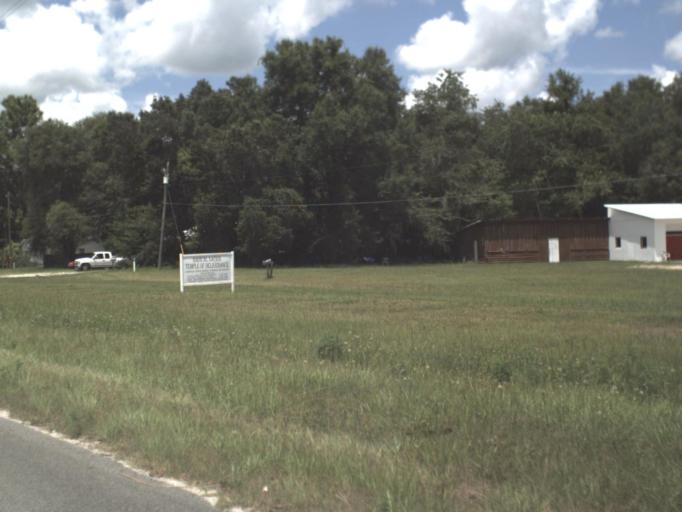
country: US
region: Florida
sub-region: Taylor County
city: Perry
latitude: 30.1088
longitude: -83.5977
